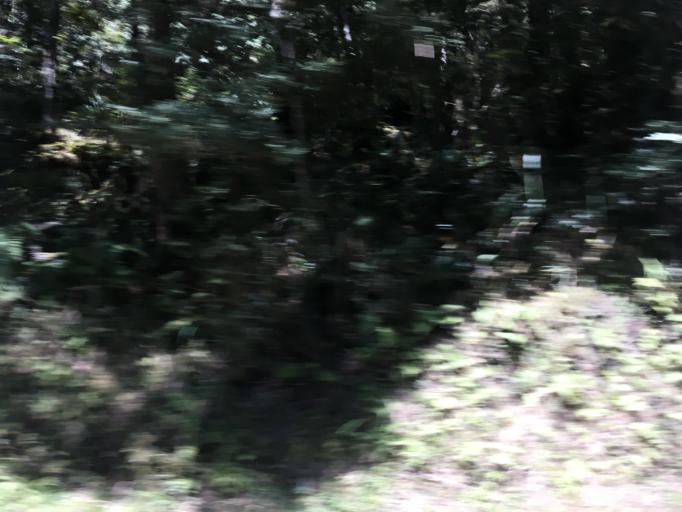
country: TW
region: Taiwan
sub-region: Yilan
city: Yilan
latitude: 24.5188
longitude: 121.5217
